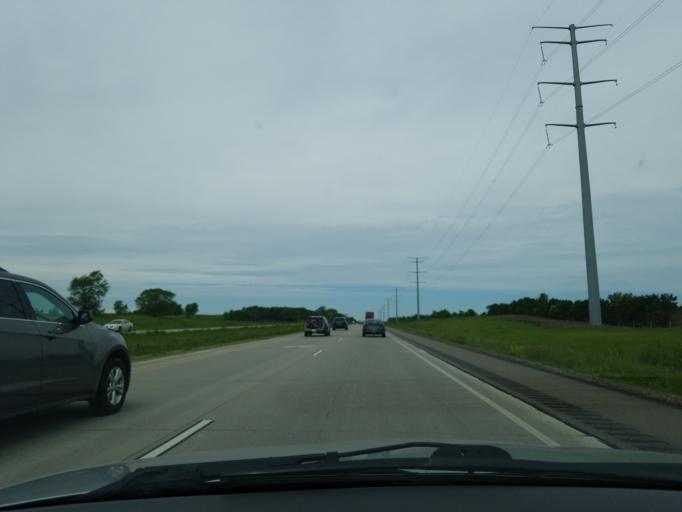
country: US
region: Minnesota
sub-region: Wright County
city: Clearwater
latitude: 45.4259
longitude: -94.0867
